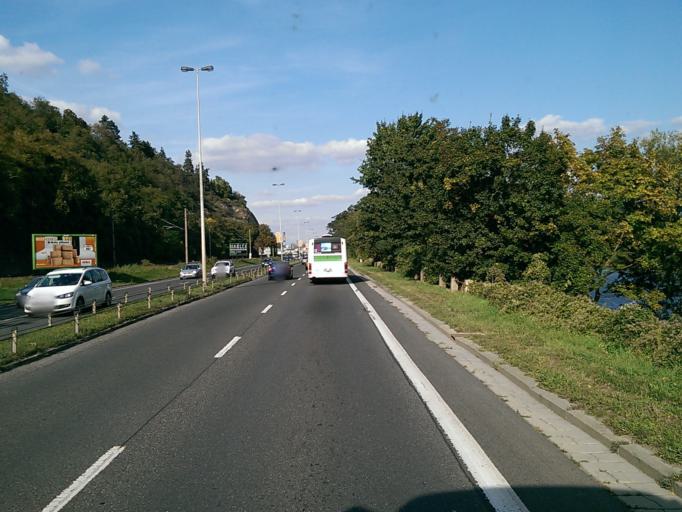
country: CZ
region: Praha
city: Branik
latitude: 50.0310
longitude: 14.3994
